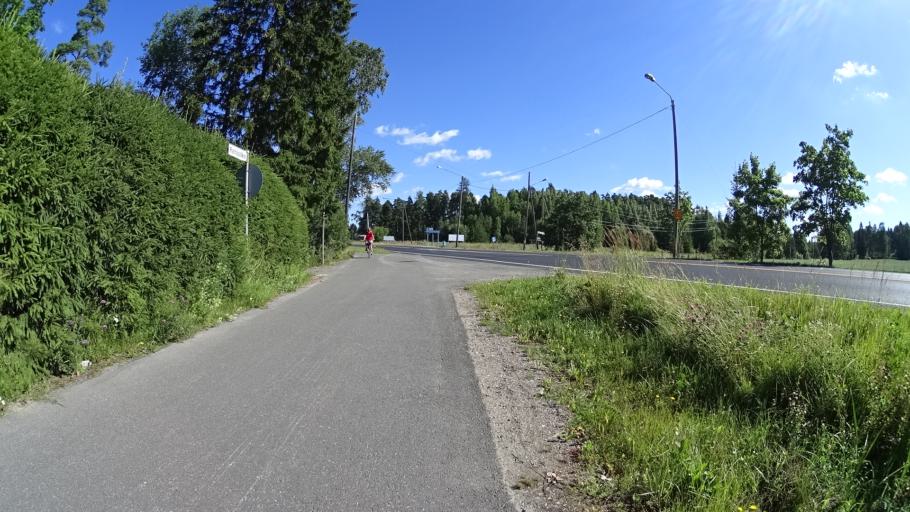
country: FI
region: Uusimaa
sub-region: Helsinki
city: Jaervenpaeae
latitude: 60.4445
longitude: 25.0767
